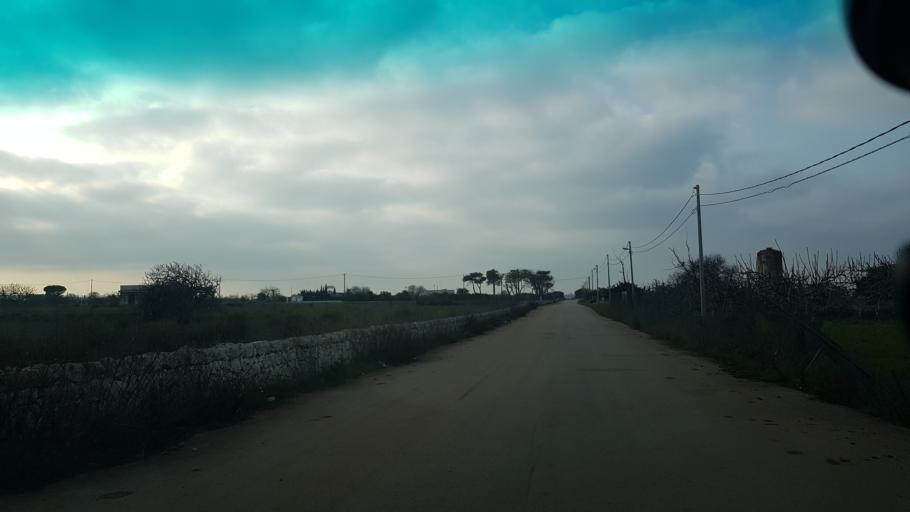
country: IT
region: Apulia
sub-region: Provincia di Brindisi
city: Carovigno
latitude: 40.7427
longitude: 17.7288
